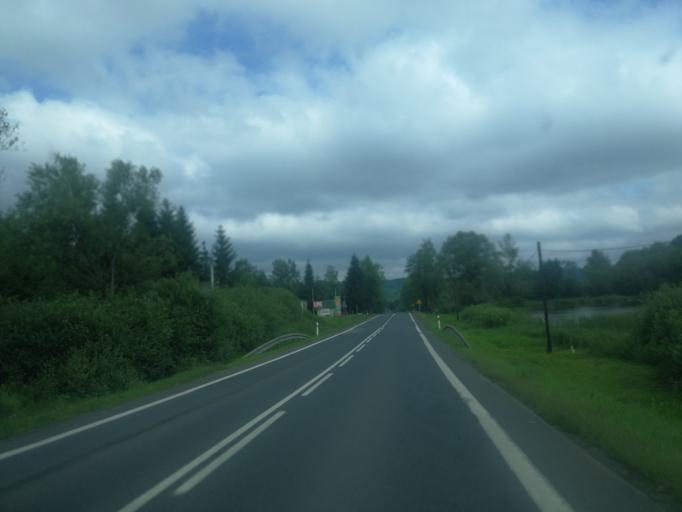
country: PL
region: Subcarpathian Voivodeship
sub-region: Powiat leski
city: Lesko
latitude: 49.4881
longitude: 22.3224
